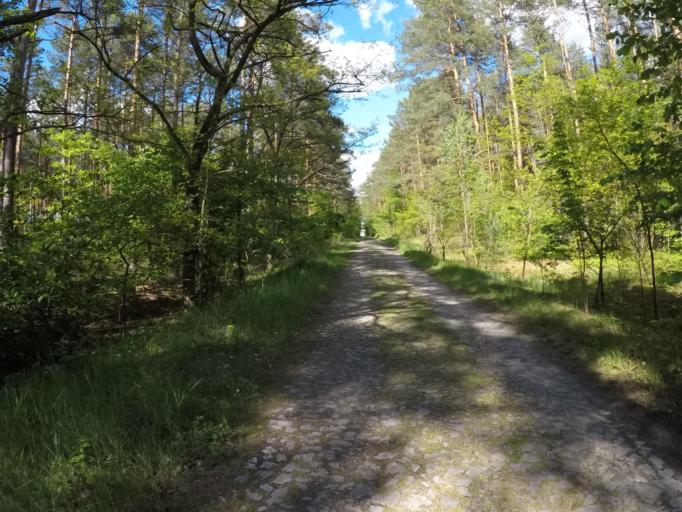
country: PL
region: Swietokrzyskie
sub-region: Powiat kielecki
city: Kostomloty Drugie
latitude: 50.8944
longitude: 20.5454
